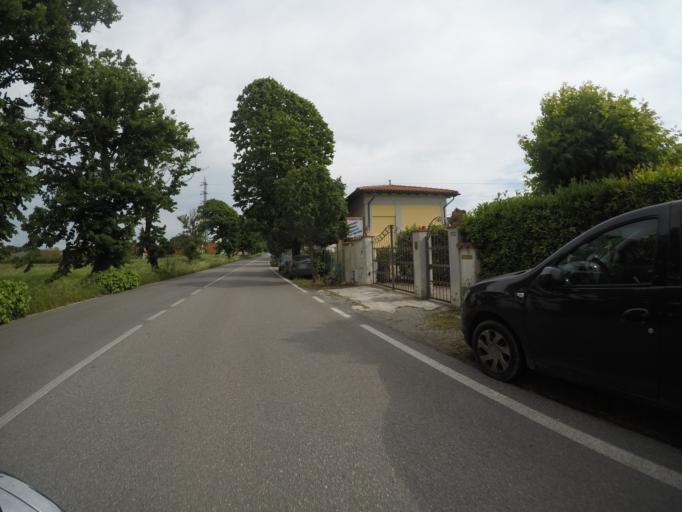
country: IT
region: Tuscany
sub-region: Province of Pisa
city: Madonna dell'Acqua
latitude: 43.7382
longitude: 10.3818
